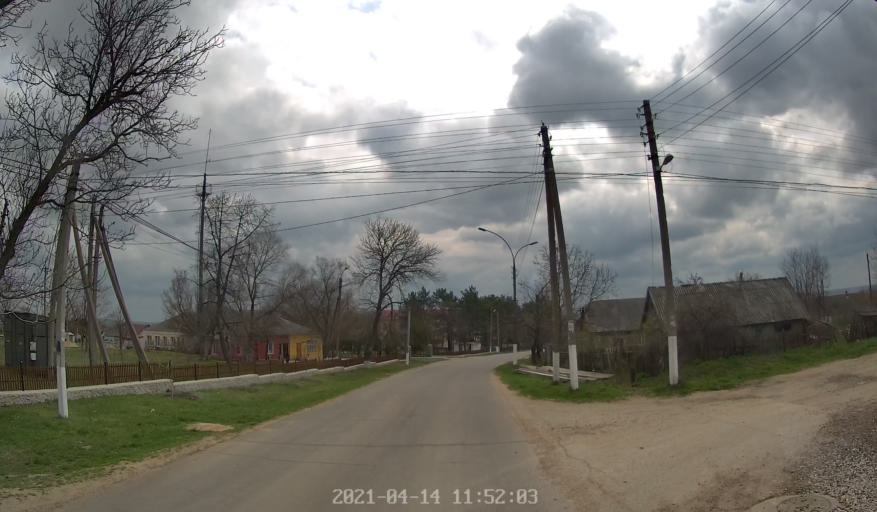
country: MD
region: Criuleni
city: Criuleni
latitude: 47.1709
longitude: 29.1945
